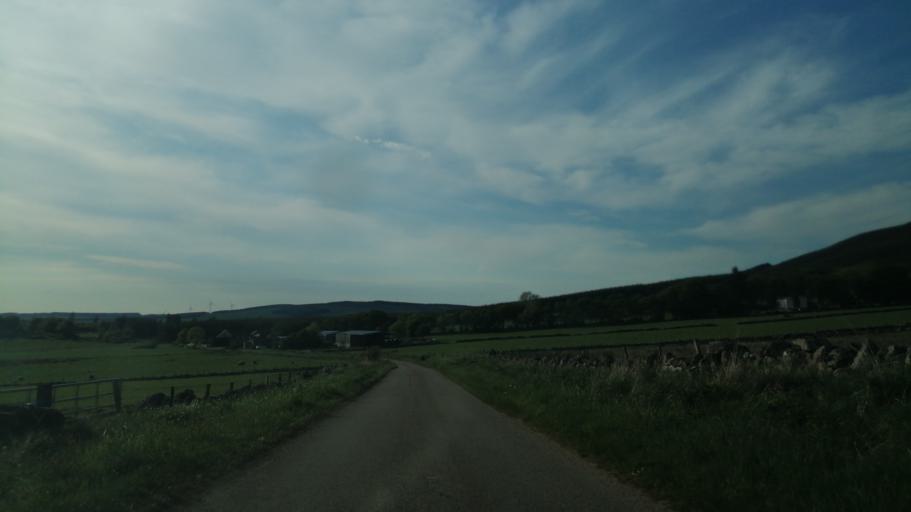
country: GB
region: Scotland
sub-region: Moray
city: Cullen
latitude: 57.5730
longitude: -2.7827
